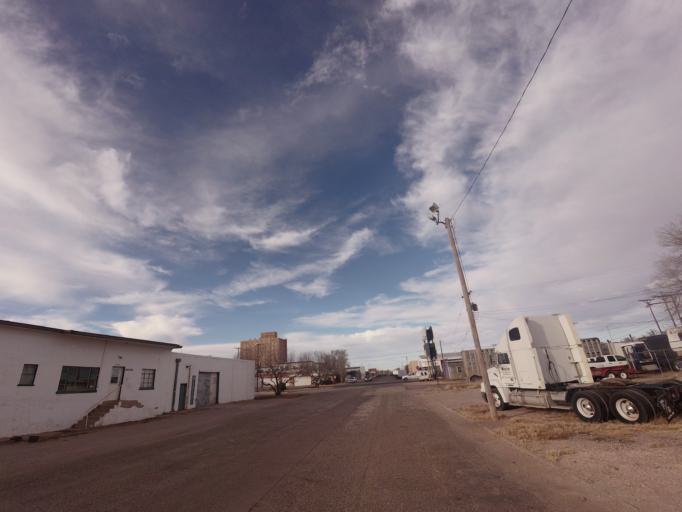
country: US
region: New Mexico
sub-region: Curry County
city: Clovis
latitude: 34.3979
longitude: -103.2040
